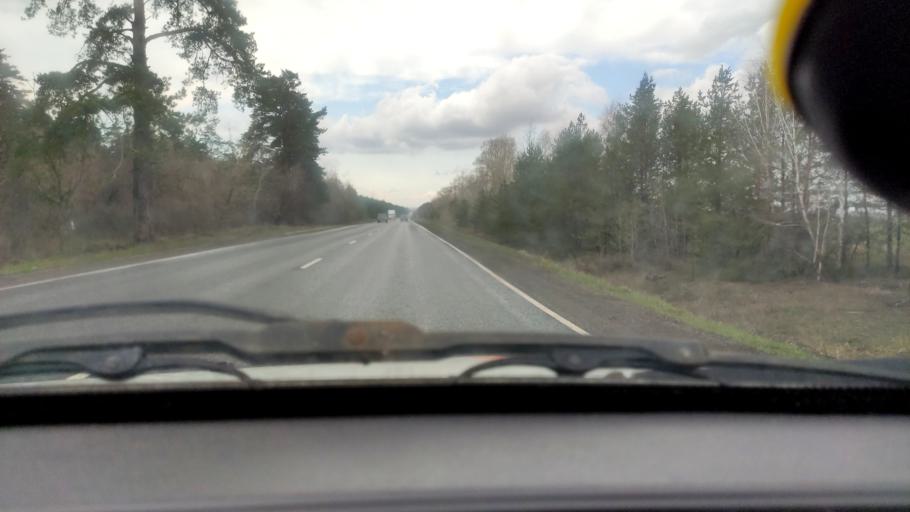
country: RU
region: Samara
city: Povolzhskiy
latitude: 53.6202
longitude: 49.6394
